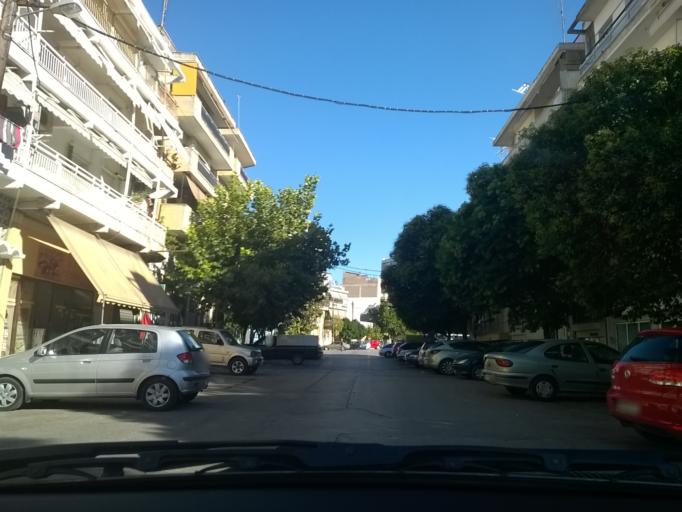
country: GR
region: Central Macedonia
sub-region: Nomos Thessalonikis
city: Ampelokipoi
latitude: 40.6494
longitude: 22.9306
